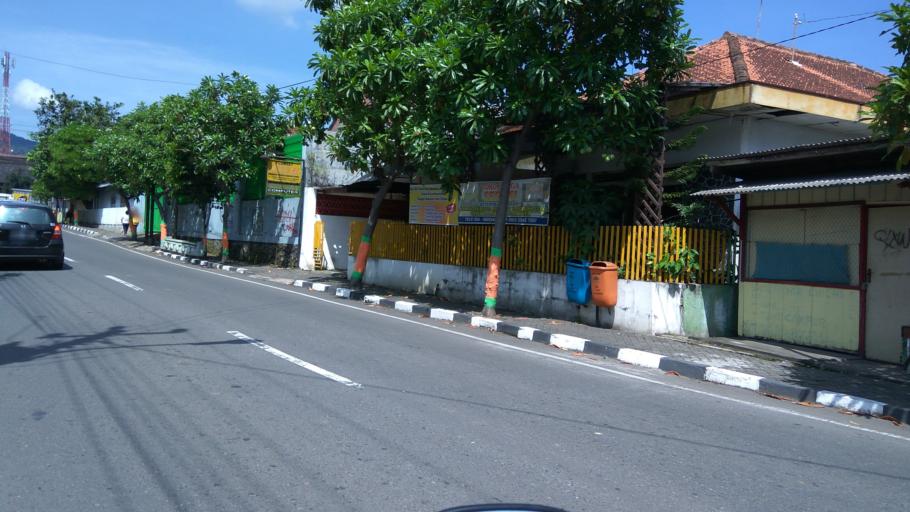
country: ID
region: Central Java
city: Ungaran
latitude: -7.1377
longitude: 110.4059
